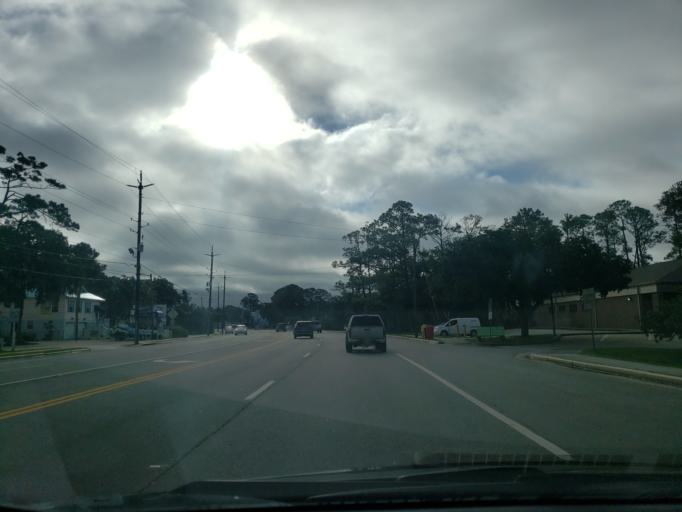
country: US
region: Georgia
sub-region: Chatham County
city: Tybee Island
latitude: 32.0157
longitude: -80.8485
